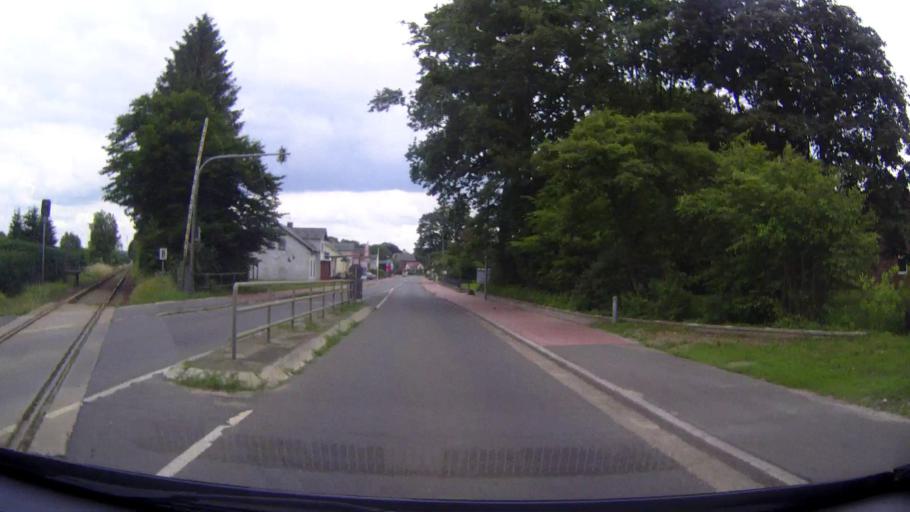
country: DE
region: Schleswig-Holstein
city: Hanerau-Hademarschen
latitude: 54.1225
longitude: 9.4249
